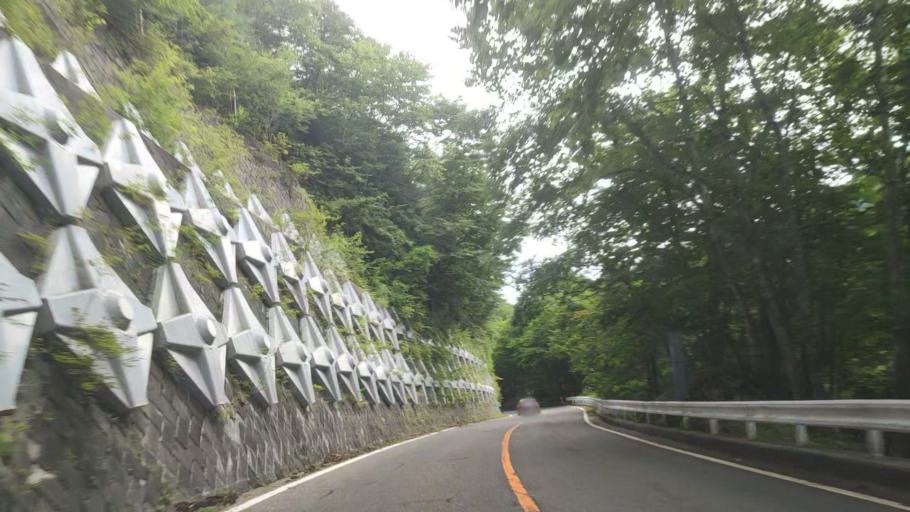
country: JP
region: Tochigi
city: Nikko
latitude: 36.8064
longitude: 139.4267
